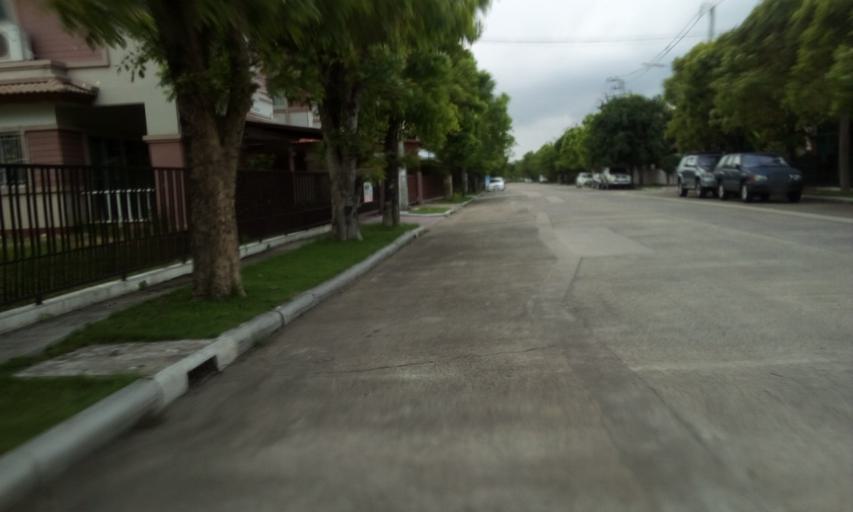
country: TH
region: Pathum Thani
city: Ban Rangsit
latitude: 14.0480
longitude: 100.8287
